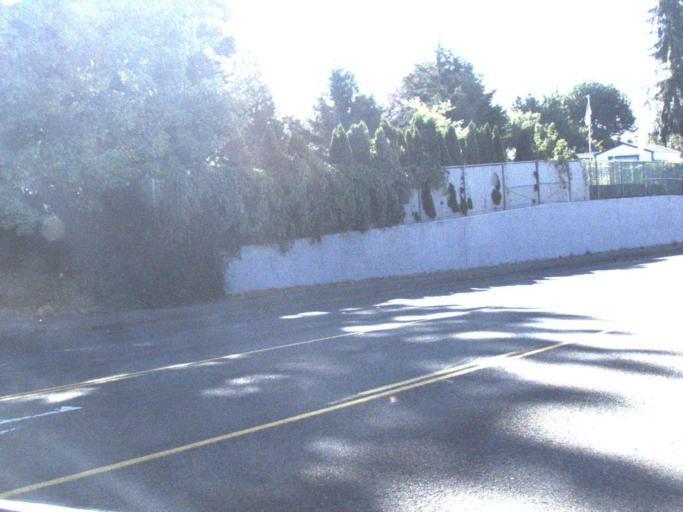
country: US
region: Washington
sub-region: King County
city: East Hill-Meridian
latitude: 47.3970
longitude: -122.2022
